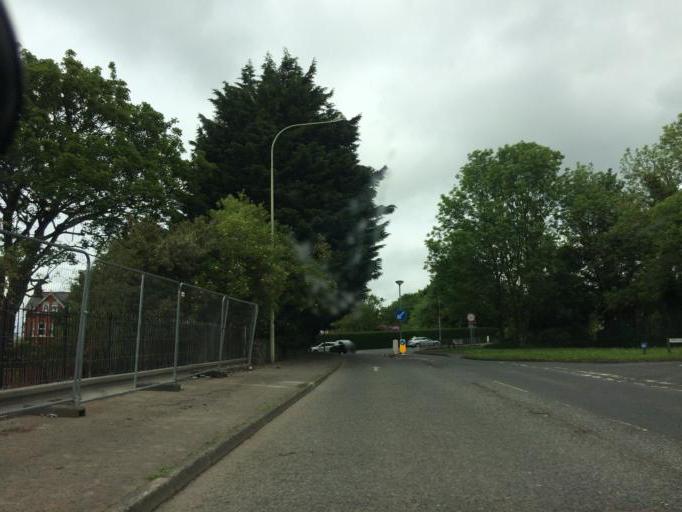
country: GB
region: Northern Ireland
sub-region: Antrim Borough
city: Antrim
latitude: 54.7127
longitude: -6.2098
